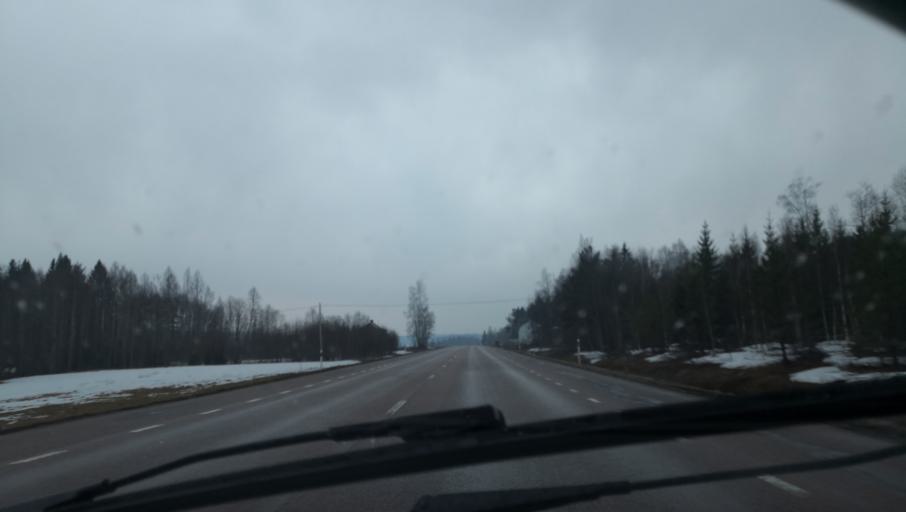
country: SE
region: Gaevleborg
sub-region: Nordanstigs Kommun
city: Bergsjoe
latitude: 62.0235
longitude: 17.2531
